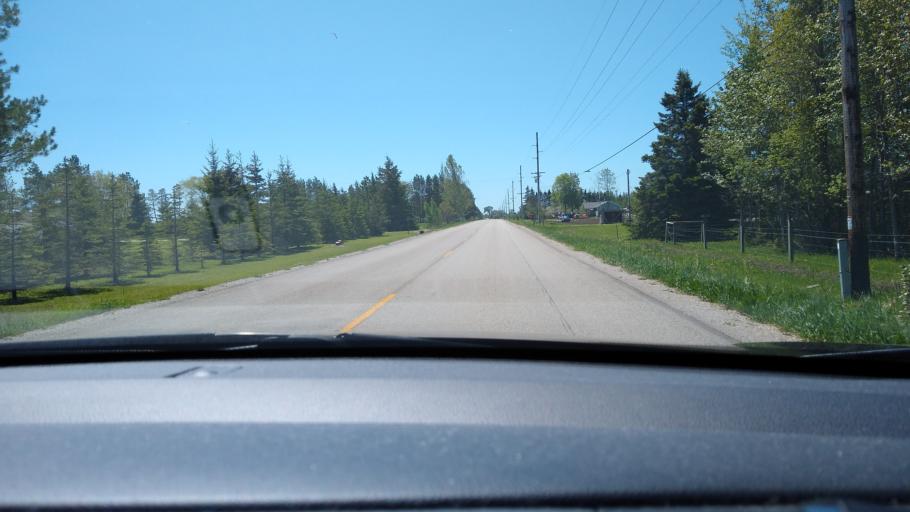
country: US
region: Michigan
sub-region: Delta County
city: Escanaba
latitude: 45.8509
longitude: -87.1841
